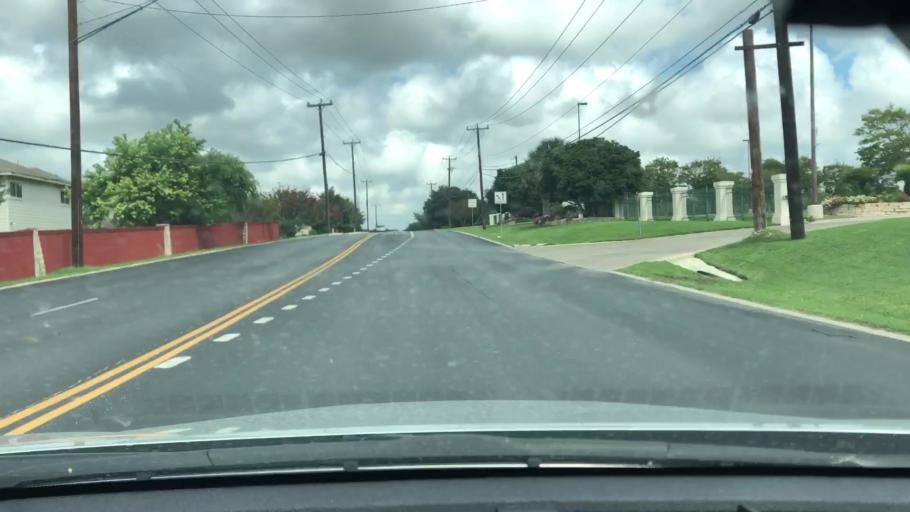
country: US
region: Texas
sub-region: Bexar County
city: Windcrest
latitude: 29.5271
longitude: -98.3693
